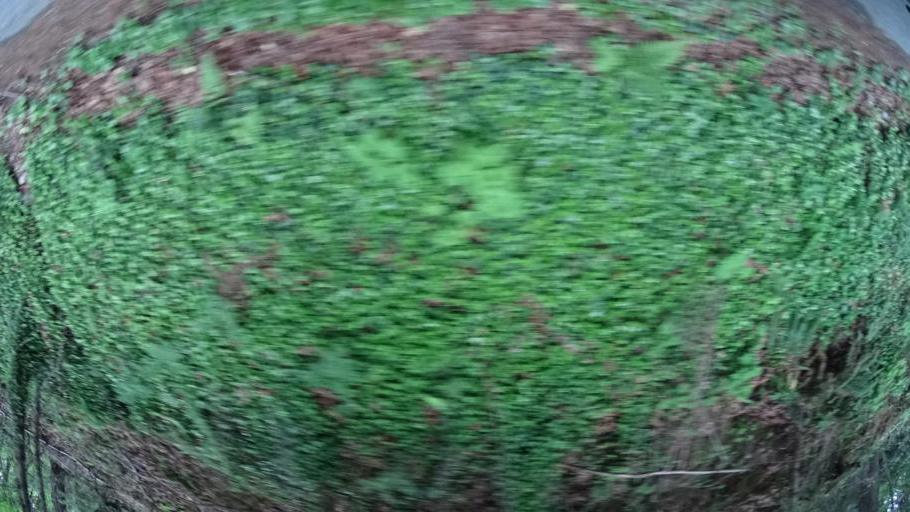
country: US
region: California
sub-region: Humboldt County
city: Willow Creek
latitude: 40.9524
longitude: -123.6301
